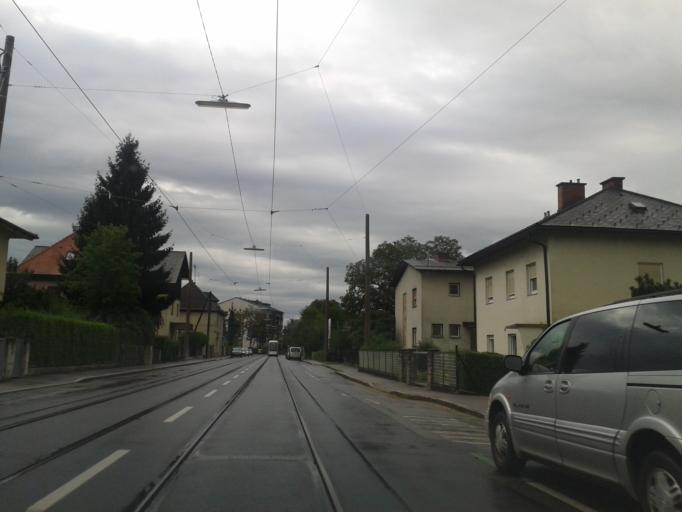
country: AT
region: Styria
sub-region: Graz Stadt
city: Goesting
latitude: 47.0920
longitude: 15.4256
